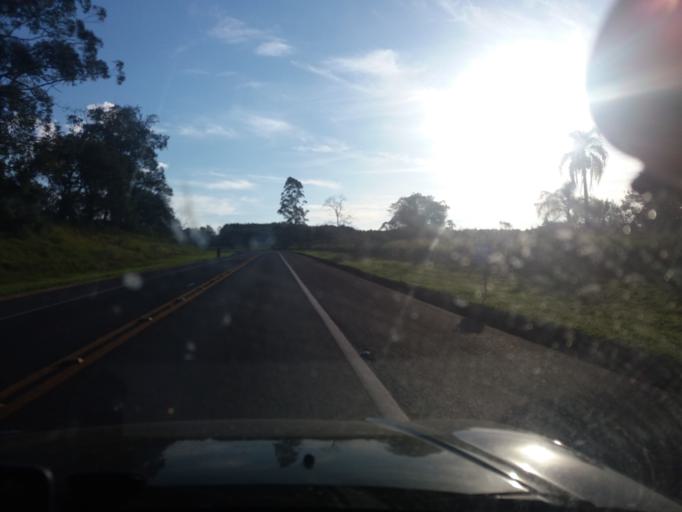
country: BR
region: Sao Paulo
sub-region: Buri
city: Buri
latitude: -23.9276
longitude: -48.6599
